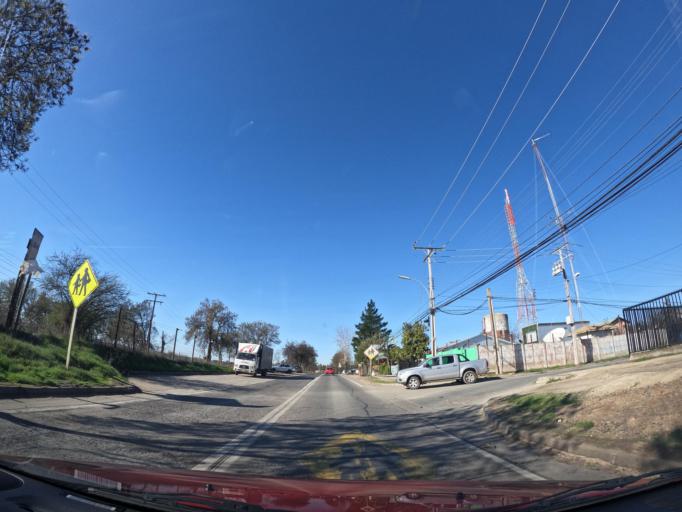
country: CL
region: Maule
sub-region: Provincia de Cauquenes
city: Cauquenes
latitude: -35.9576
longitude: -72.3007
